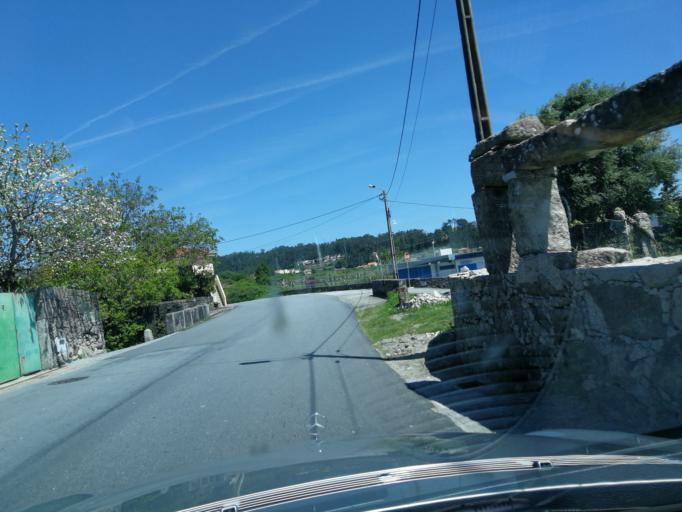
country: PT
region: Viana do Castelo
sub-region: Viana do Castelo
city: Meadela
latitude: 41.7213
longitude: -8.7955
